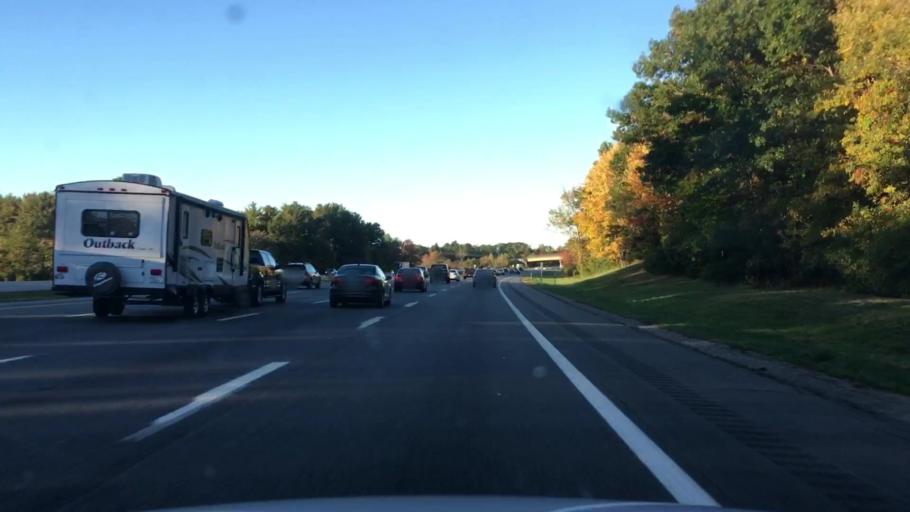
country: US
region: New Hampshire
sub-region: Rockingham County
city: North Hampton
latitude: 42.9872
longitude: -70.8509
